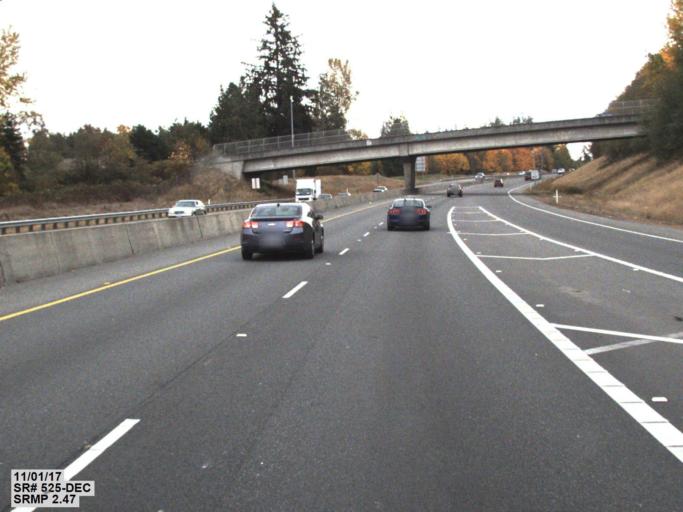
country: US
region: Washington
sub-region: Snohomish County
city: Martha Lake
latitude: 47.8654
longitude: -122.2752
